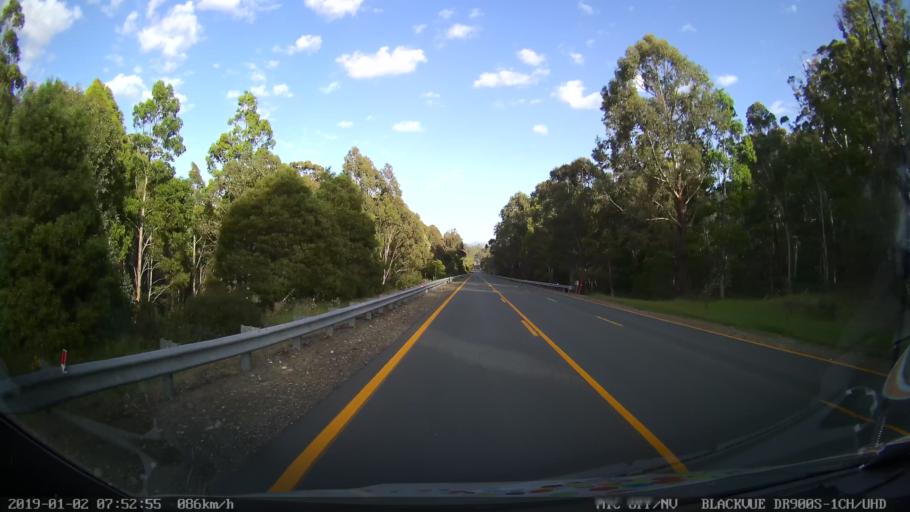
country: AU
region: New South Wales
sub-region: Tumut Shire
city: Tumut
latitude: -35.7111
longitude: 148.5125
